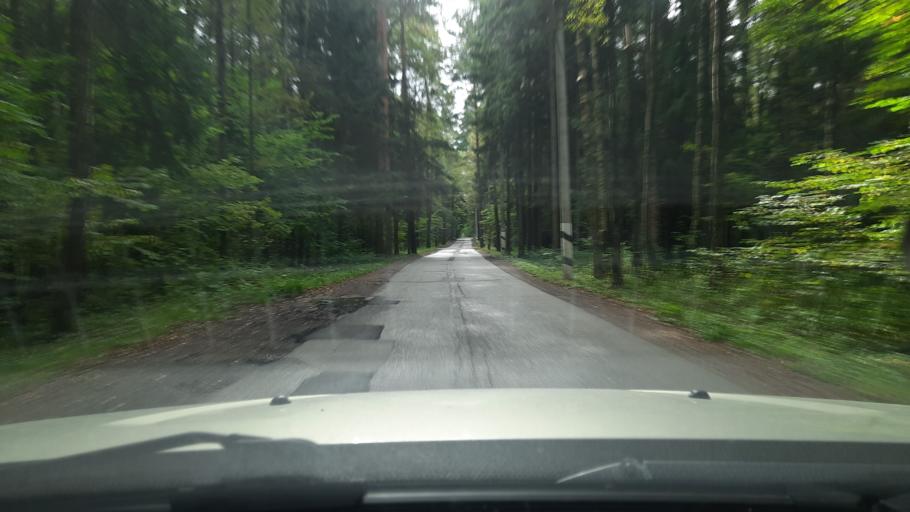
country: RU
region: Moskovskaya
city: Barvikha
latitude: 55.7199
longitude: 37.3032
